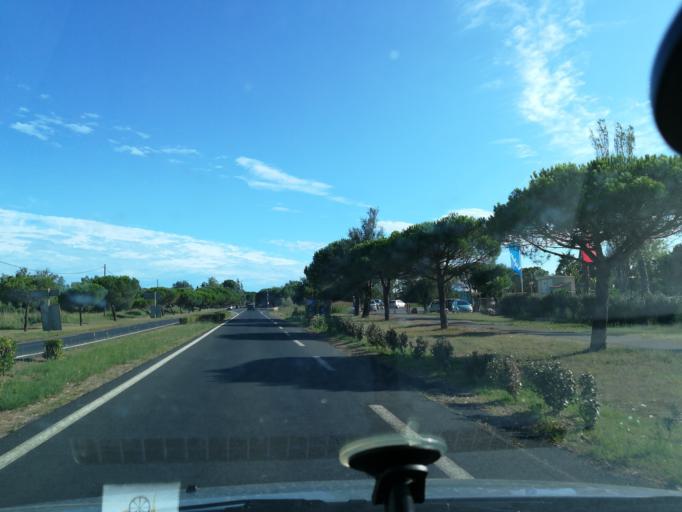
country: FR
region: Languedoc-Roussillon
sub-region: Departement de l'Herault
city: Portiragnes
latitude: 43.2883
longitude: 3.3626
